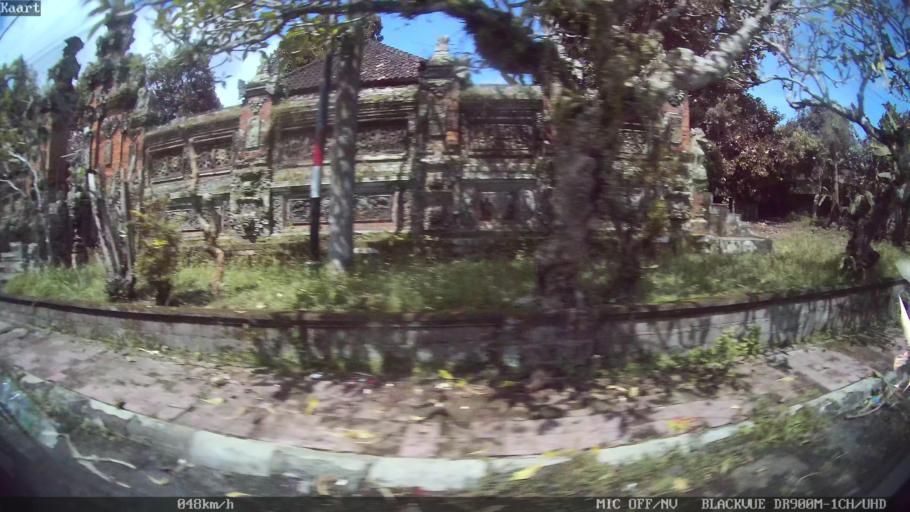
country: ID
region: Bali
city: Banjar Kelodan
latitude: -8.5271
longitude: 115.3289
